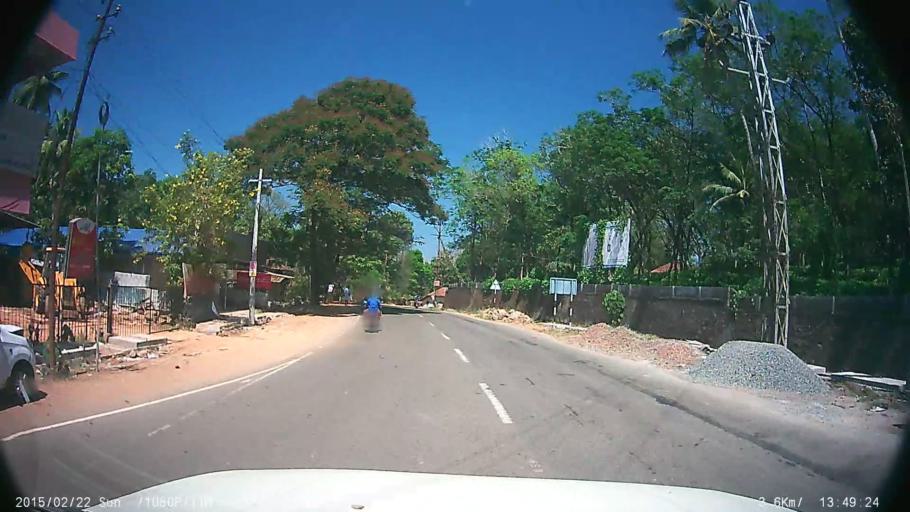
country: IN
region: Kerala
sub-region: Kottayam
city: Changanacheri
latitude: 9.5001
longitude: 76.6333
